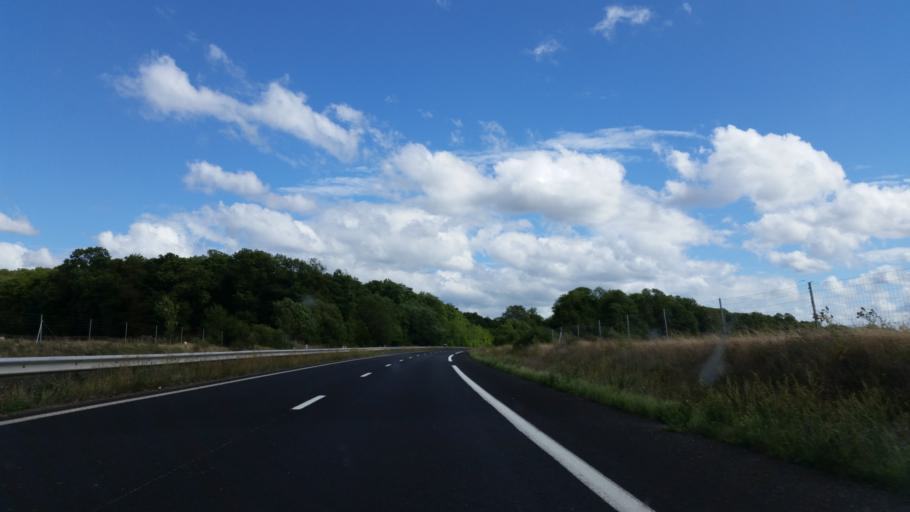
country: FR
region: Lorraine
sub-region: Departement de Meurthe-et-Moselle
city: Flavigny-sur-Moselle
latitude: 48.5469
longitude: 6.1993
